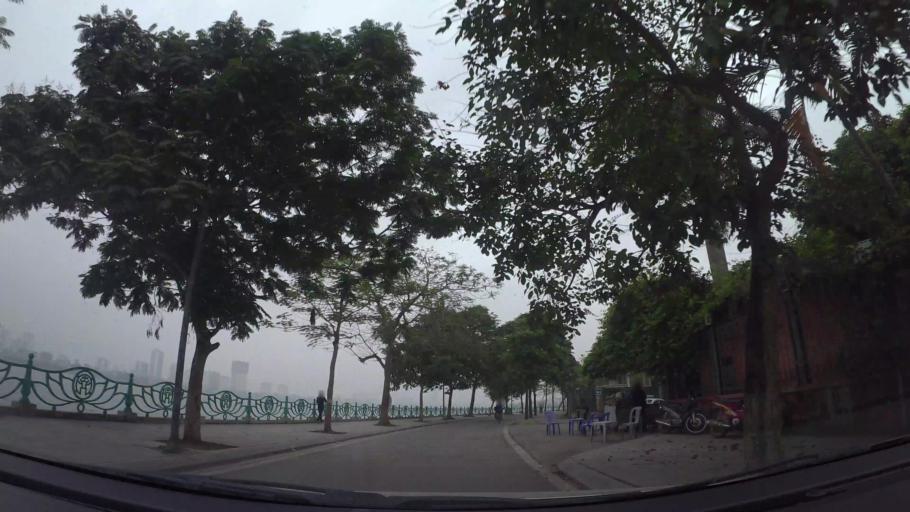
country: VN
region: Ha Noi
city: Tay Ho
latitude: 21.0597
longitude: 105.8184
